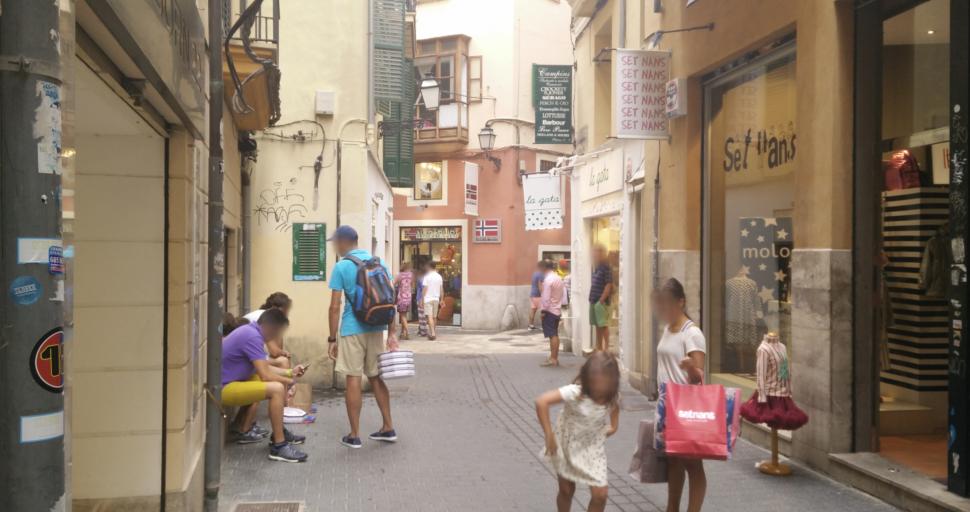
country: ES
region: Balearic Islands
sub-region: Illes Balears
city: Palma
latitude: 39.5706
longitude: 2.6471
